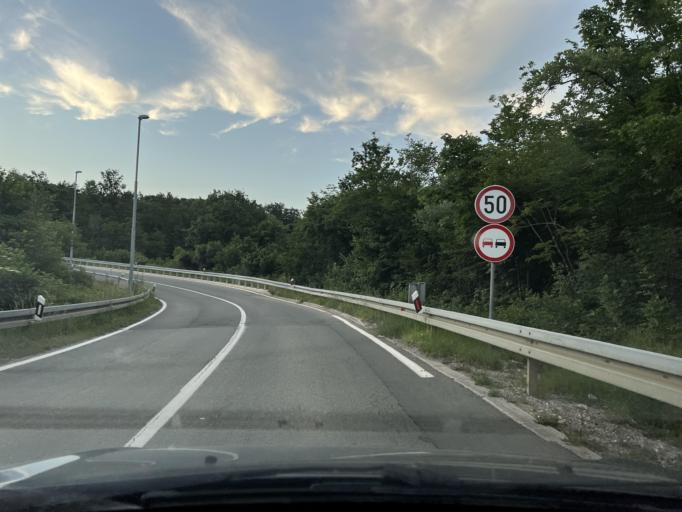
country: HR
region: Primorsko-Goranska
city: Marcelji
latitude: 45.4008
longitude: 14.3917
